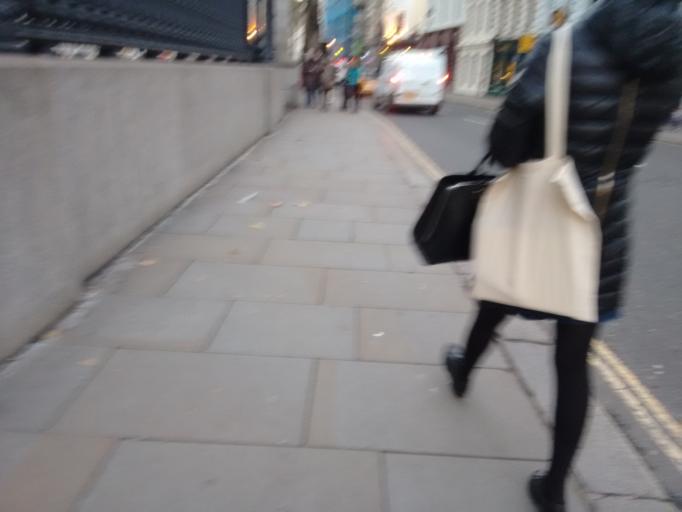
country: GB
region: England
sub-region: Greater London
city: London
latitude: 51.5180
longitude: -0.1268
